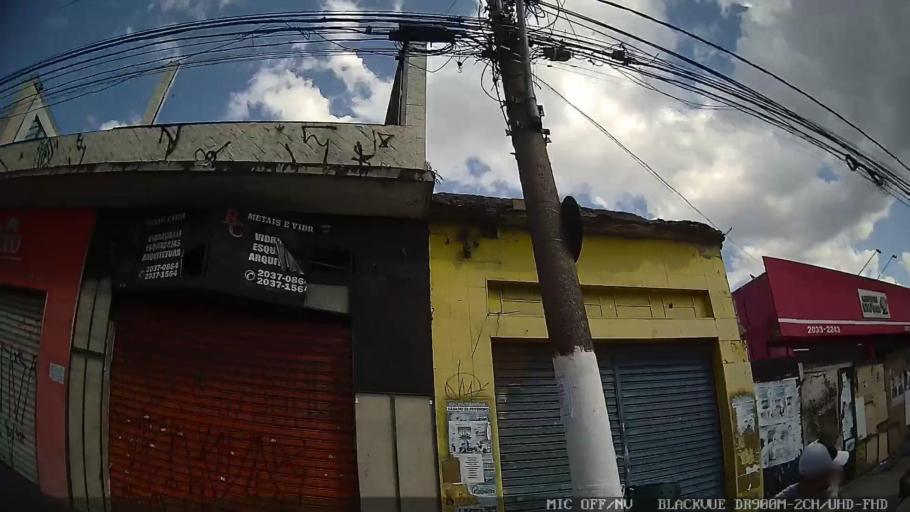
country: BR
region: Sao Paulo
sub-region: Guarulhos
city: Guarulhos
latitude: -23.4936
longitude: -46.4500
